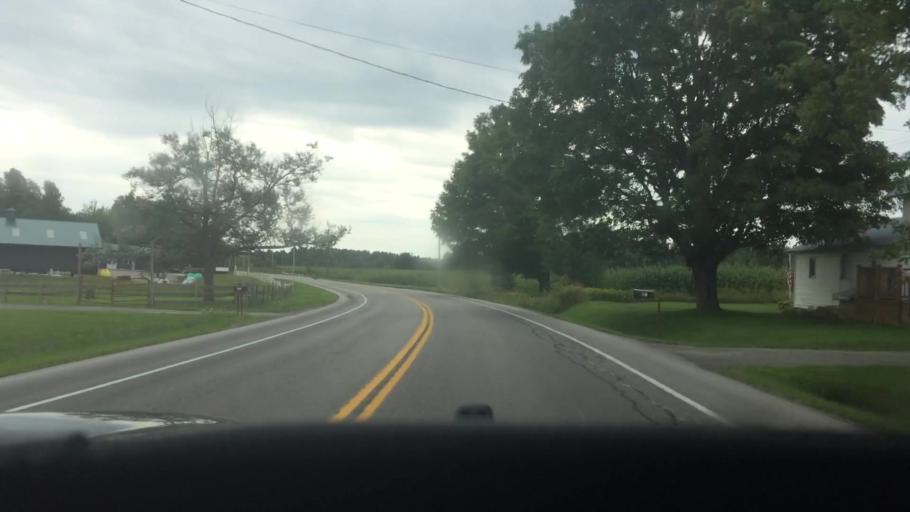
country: US
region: New York
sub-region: St. Lawrence County
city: Ogdensburg
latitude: 44.5841
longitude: -75.3713
